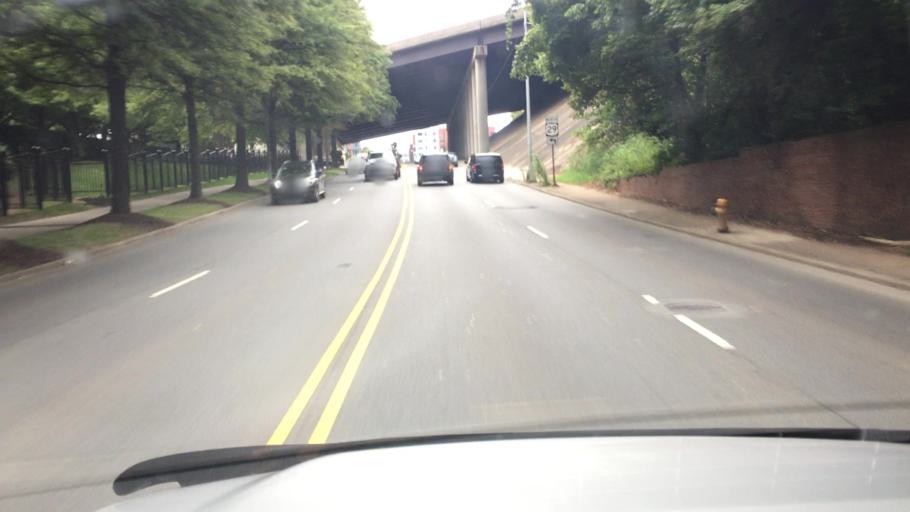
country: US
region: North Carolina
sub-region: Mecklenburg County
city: Charlotte
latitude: 35.2253
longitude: -80.8555
